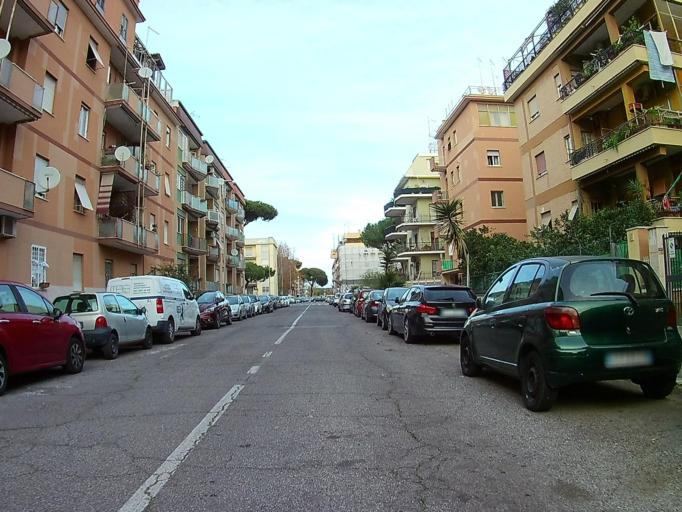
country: IT
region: Latium
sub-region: Citta metropolitana di Roma Capitale
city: Lido di Ostia
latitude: 41.7352
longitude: 12.2861
